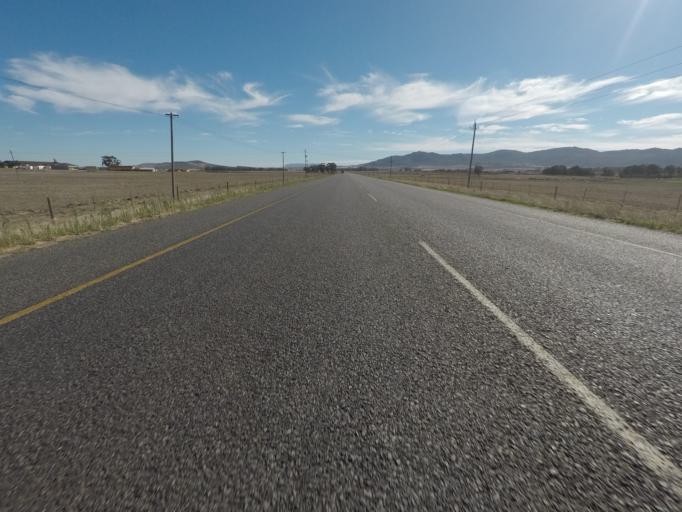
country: ZA
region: Western Cape
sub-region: West Coast District Municipality
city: Malmesbury
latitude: -33.6373
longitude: 18.7184
